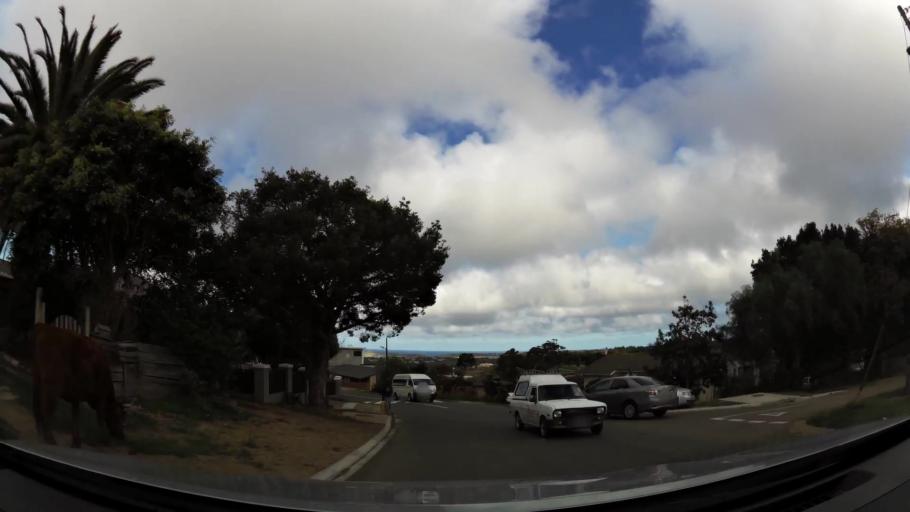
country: ZA
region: Western Cape
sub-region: Eden District Municipality
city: Plettenberg Bay
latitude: -34.0524
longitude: 23.3402
